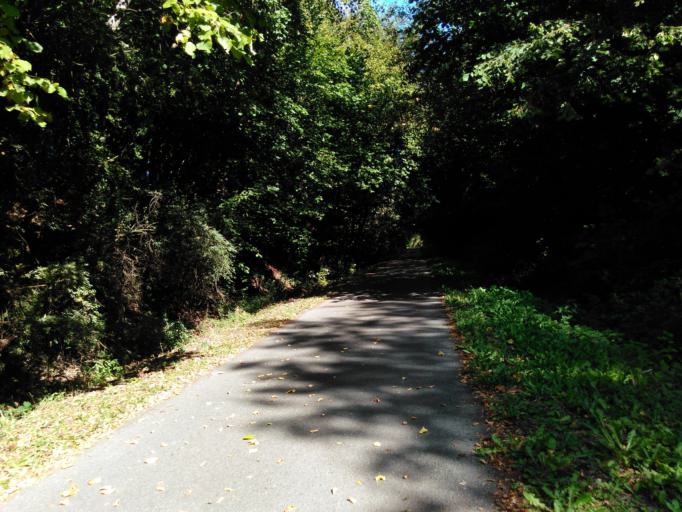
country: BE
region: Wallonia
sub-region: Province du Luxembourg
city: Bastogne
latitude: 50.0207
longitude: 5.7432
